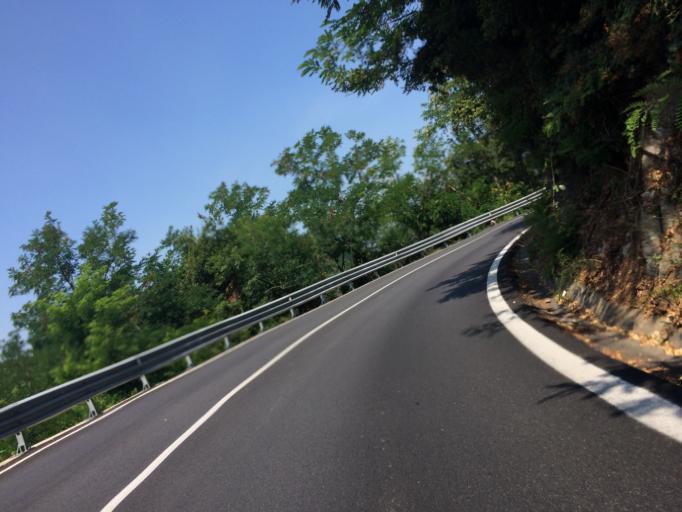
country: IT
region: Liguria
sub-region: Provincia di Genova
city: Cogoleto
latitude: 44.3969
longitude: 8.6638
